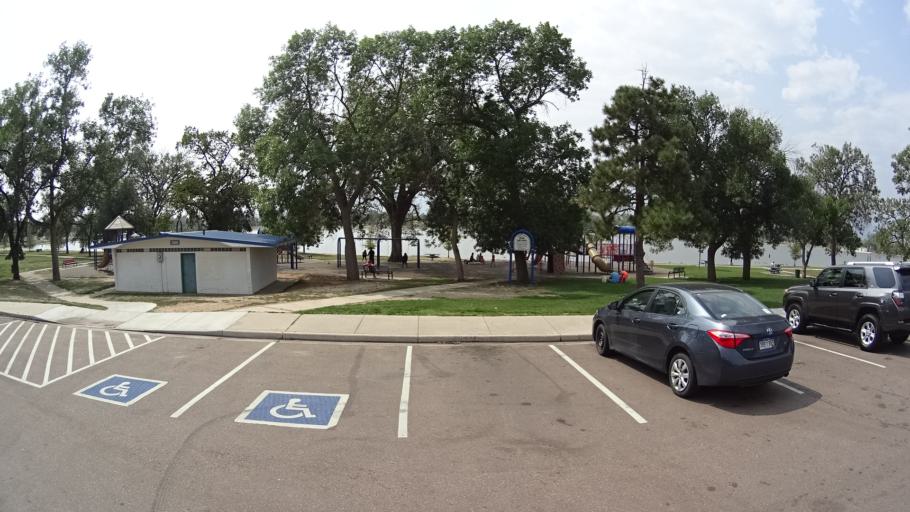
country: US
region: Colorado
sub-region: El Paso County
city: Colorado Springs
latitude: 38.8259
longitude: -104.7959
